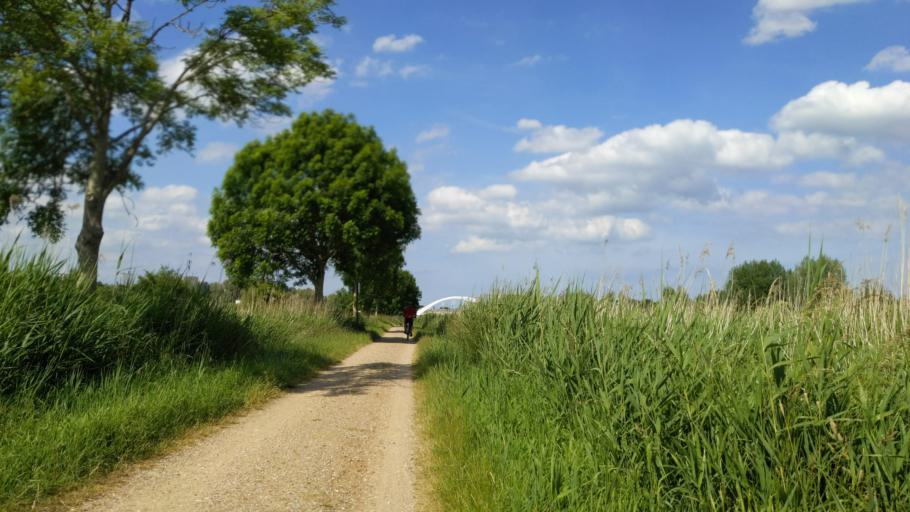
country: DE
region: Schleswig-Holstein
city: Krummesse
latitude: 53.8274
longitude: 10.6368
